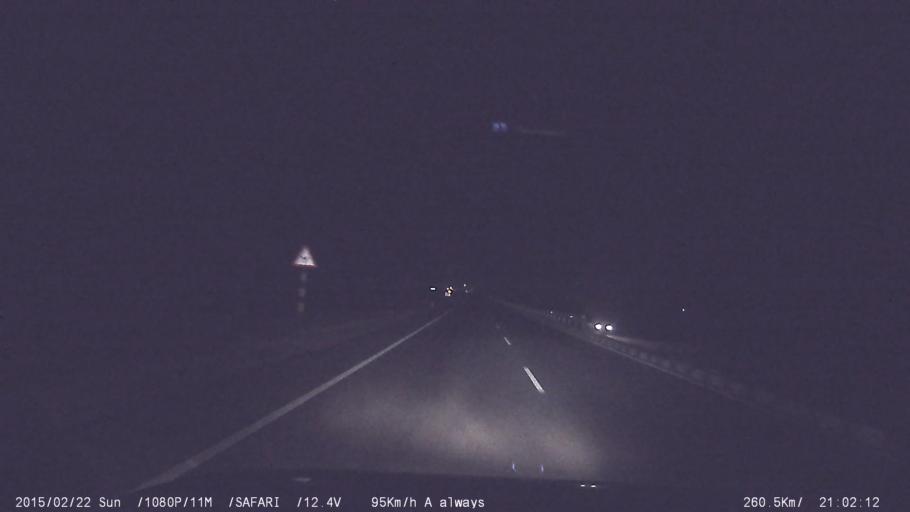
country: IN
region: Tamil Nadu
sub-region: Karur
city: Pallappatti
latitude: 10.6746
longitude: 77.9299
